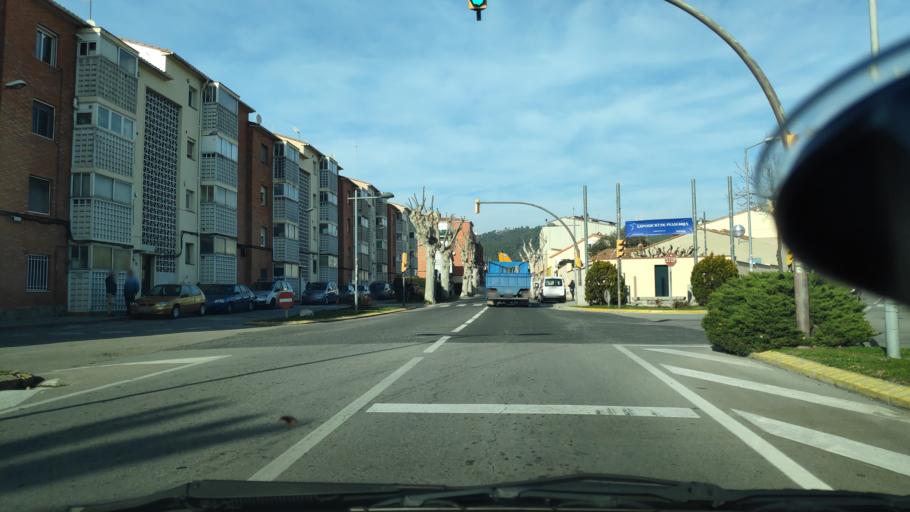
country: ES
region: Catalonia
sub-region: Provincia de Barcelona
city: Castellar del Valles
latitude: 41.6106
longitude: 2.0837
